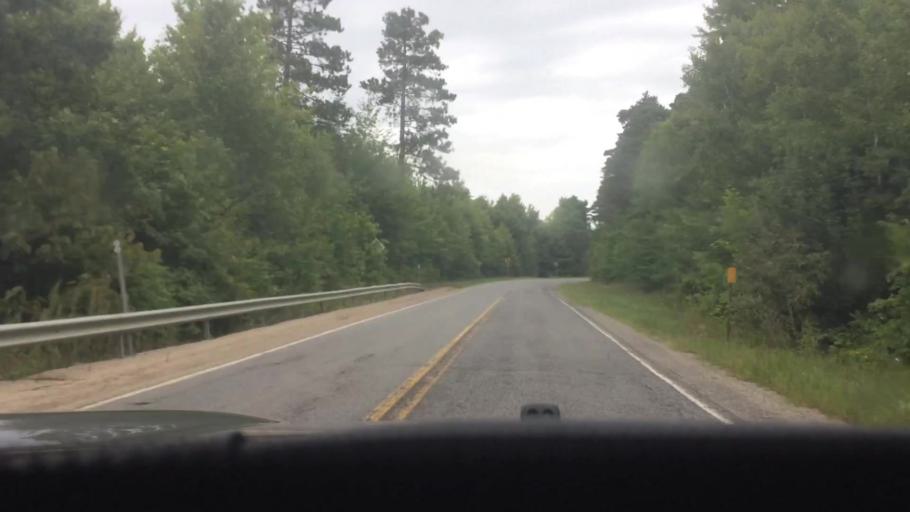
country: US
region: New York
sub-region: St. Lawrence County
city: Hannawa Falls
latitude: 44.6079
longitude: -74.8844
